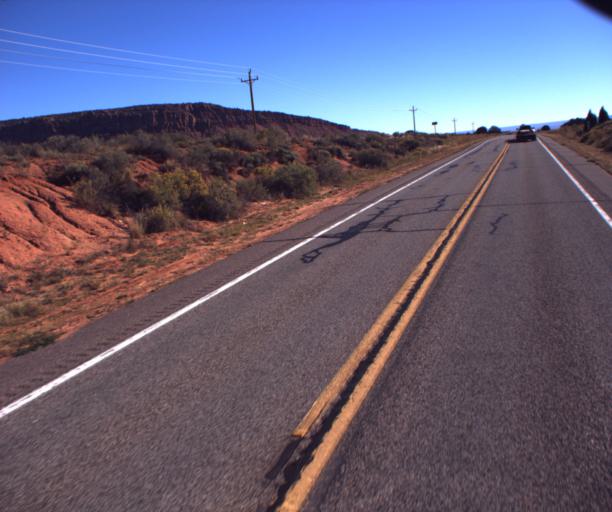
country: US
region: Arizona
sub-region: Mohave County
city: Colorado City
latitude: 36.8581
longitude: -112.7759
